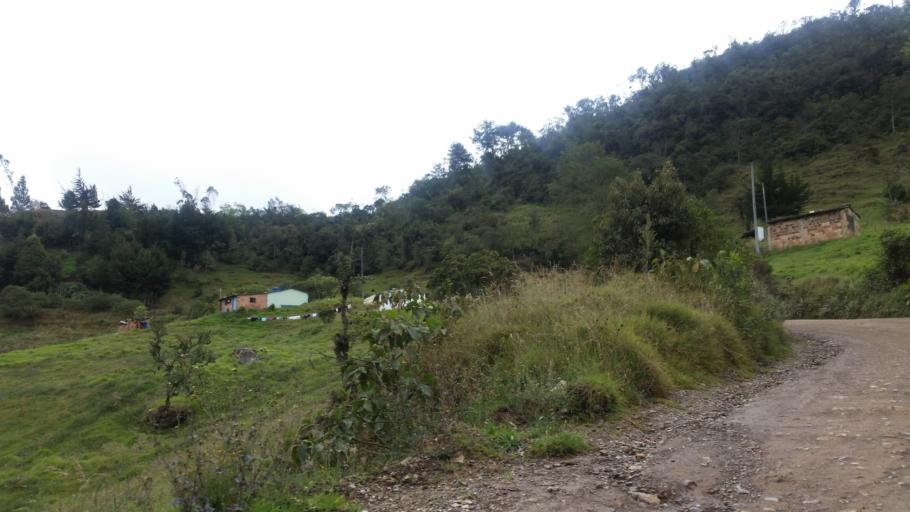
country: CO
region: Cundinamarca
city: La Calera
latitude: 4.7143
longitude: -73.9351
